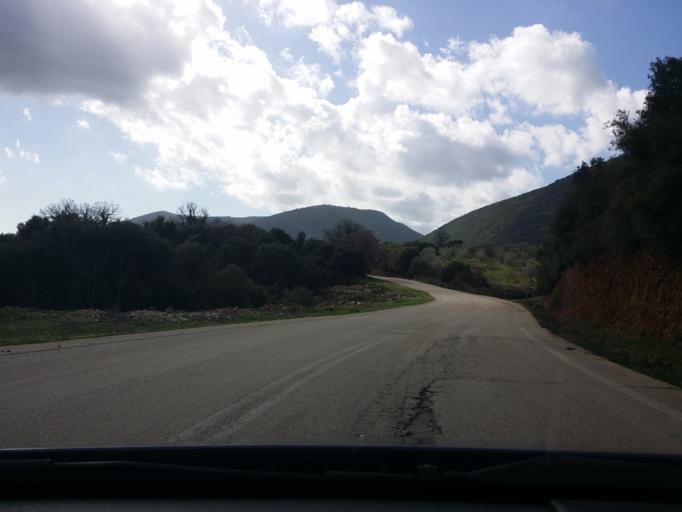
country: GR
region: West Greece
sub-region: Nomos Aitolias kai Akarnanias
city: Fitiai
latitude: 38.6243
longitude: 21.1504
